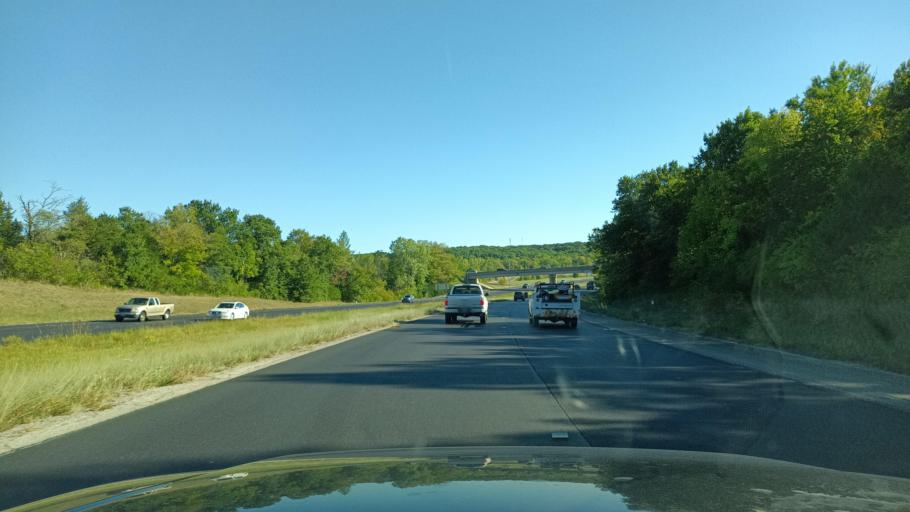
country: US
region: Missouri
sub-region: Boone County
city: Columbia
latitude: 38.9839
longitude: -92.2816
